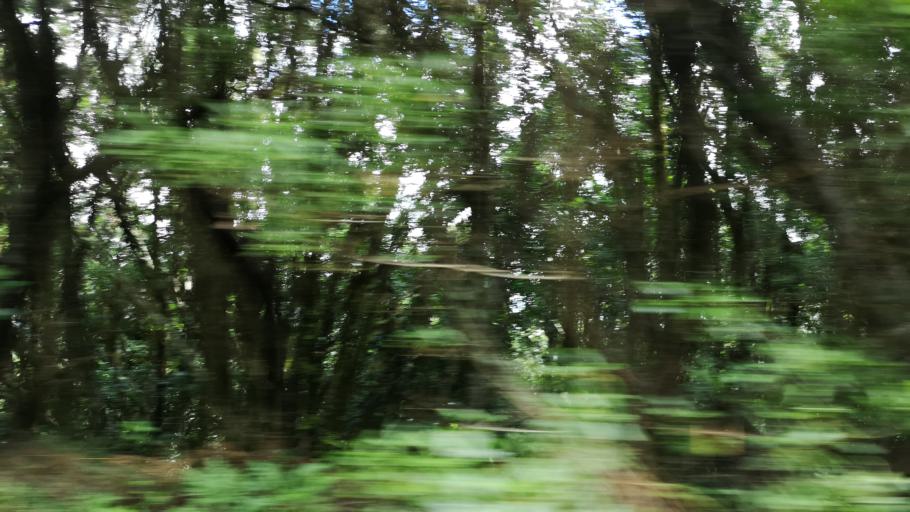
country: ES
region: Canary Islands
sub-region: Provincia de Santa Cruz de Tenerife
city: Alajero
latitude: 28.1132
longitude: -17.2181
